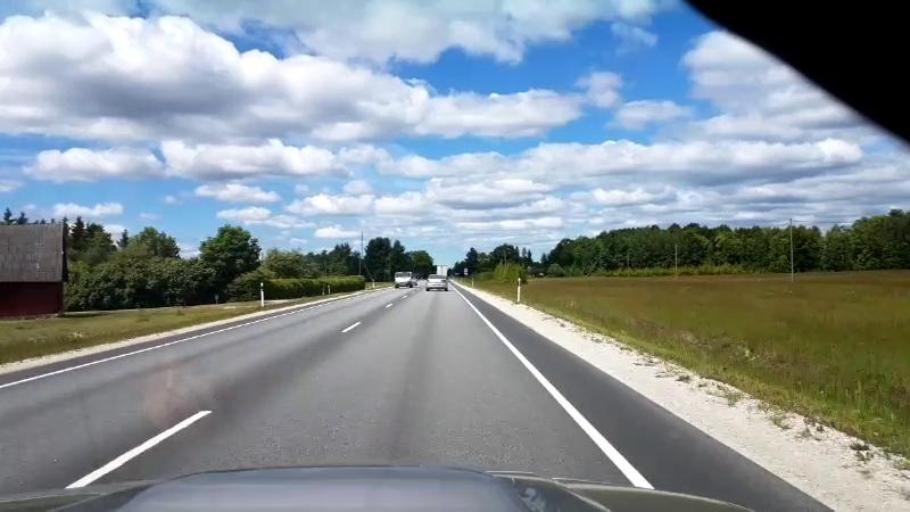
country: EE
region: Paernumaa
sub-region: Halinga vald
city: Parnu-Jaagupi
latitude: 58.6517
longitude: 24.4789
